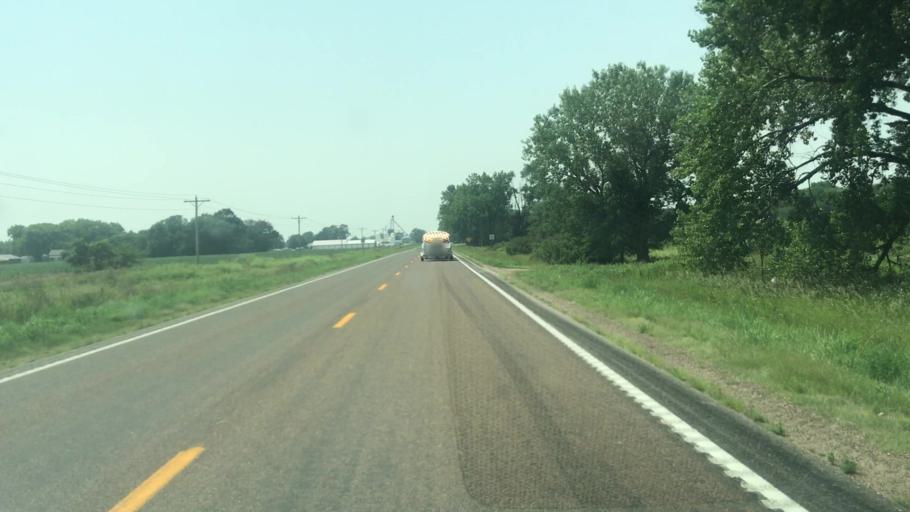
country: US
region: Nebraska
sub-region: Buffalo County
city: Ravenna
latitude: 41.0761
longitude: -98.7051
